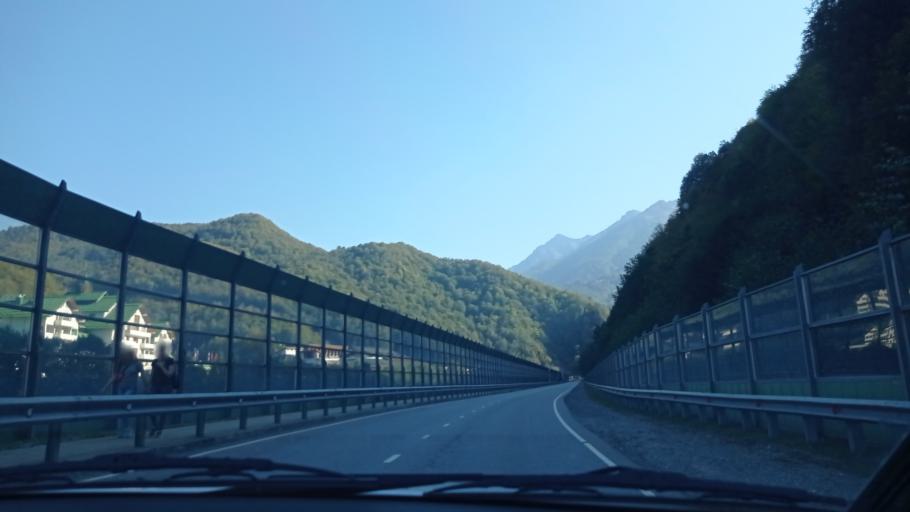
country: RU
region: Krasnodarskiy
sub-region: Sochi City
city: Krasnaya Polyana
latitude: 43.6900
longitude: 40.2735
